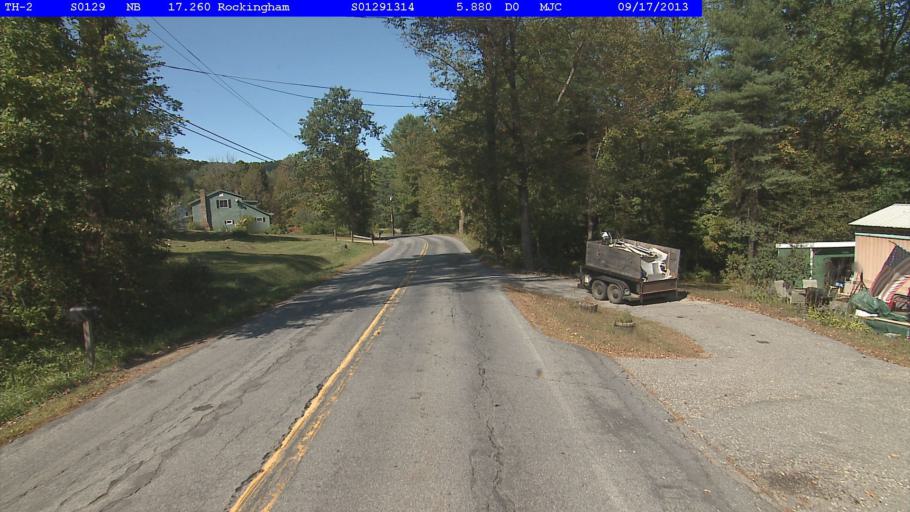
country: US
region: Vermont
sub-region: Windham County
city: Rockingham
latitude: 43.2010
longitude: -72.5129
